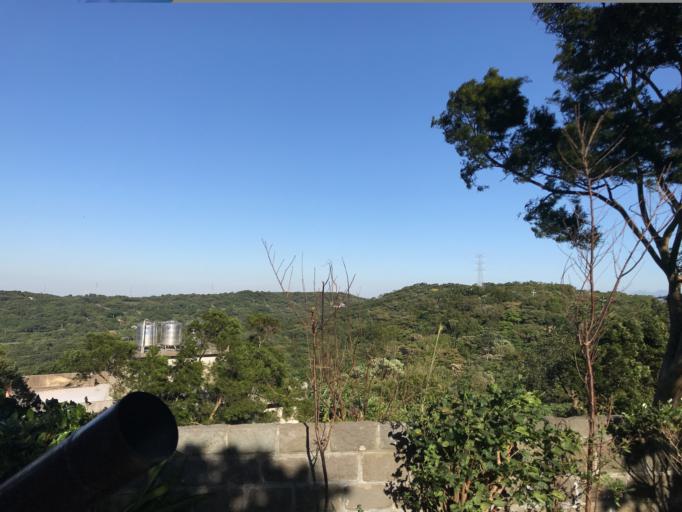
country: TW
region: Taiwan
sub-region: Hsinchu
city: Zhubei
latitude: 24.8689
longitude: 121.0915
